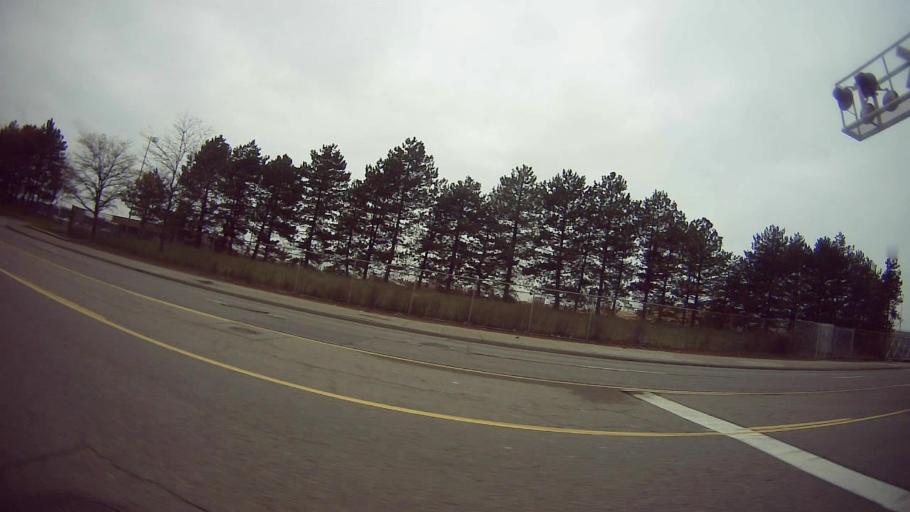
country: US
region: Michigan
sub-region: Wayne County
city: Hamtramck
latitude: 42.3829
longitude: -83.0368
